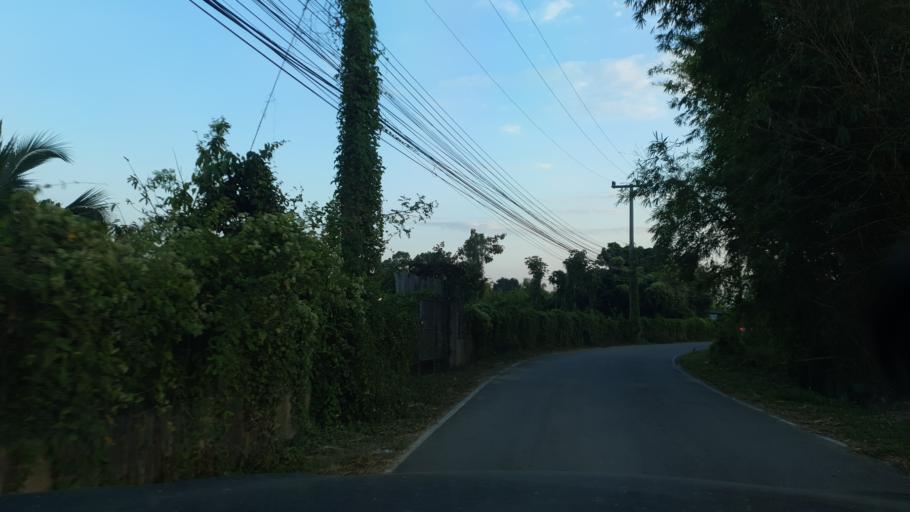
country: TH
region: Chiang Mai
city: San Sai
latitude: 18.8588
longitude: 99.0747
